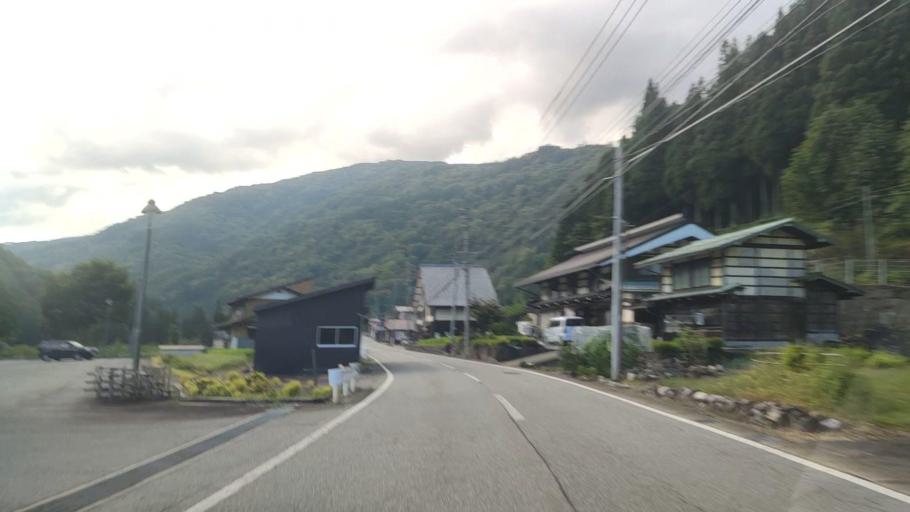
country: JP
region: Gifu
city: Takayama
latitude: 36.3052
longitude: 137.0959
